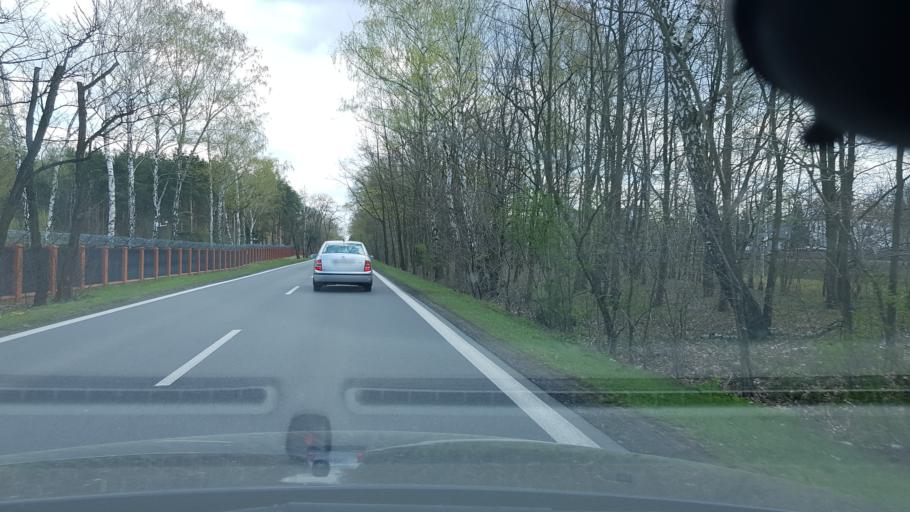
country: PL
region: Masovian Voivodeship
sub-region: Warszawa
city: Wesola
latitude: 52.2538
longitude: 21.2367
